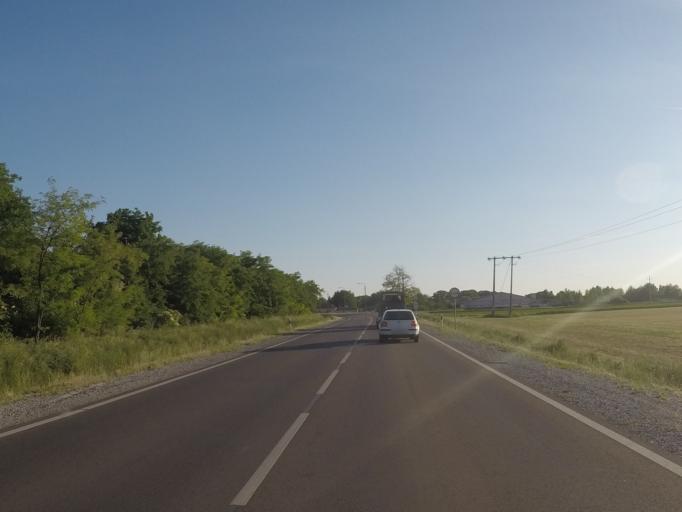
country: HU
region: Heves
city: Erdotelek
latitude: 47.6606
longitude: 20.3492
